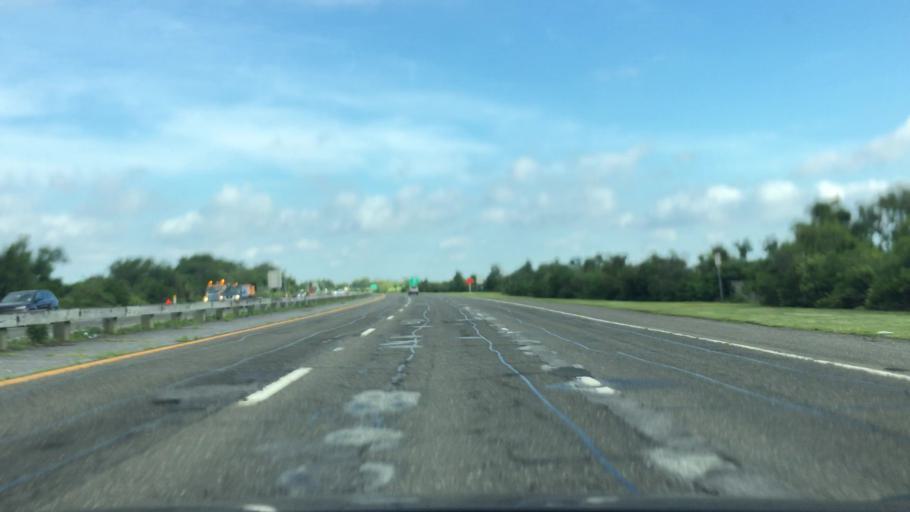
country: US
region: New York
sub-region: Nassau County
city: Point Lookout
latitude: 40.6027
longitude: -73.5441
